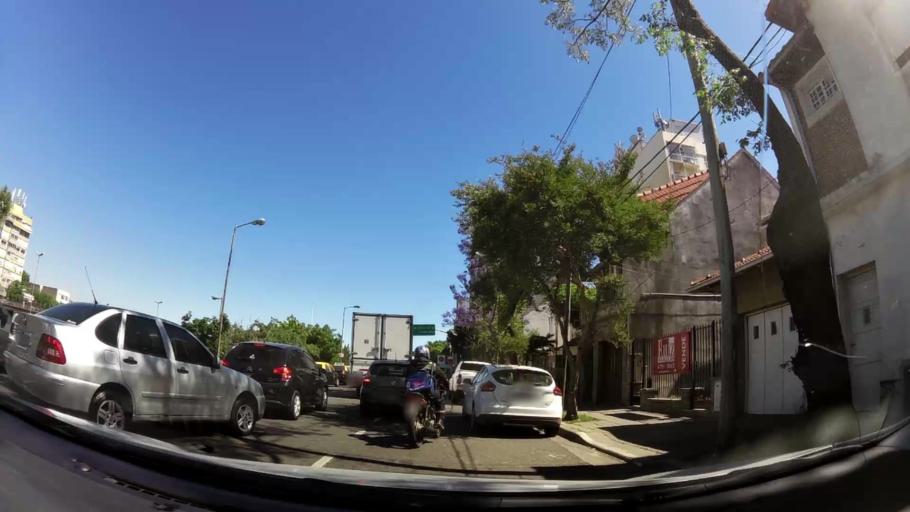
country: AR
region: Buenos Aires
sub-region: Partido de Vicente Lopez
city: Olivos
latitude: -34.5340
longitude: -58.5027
